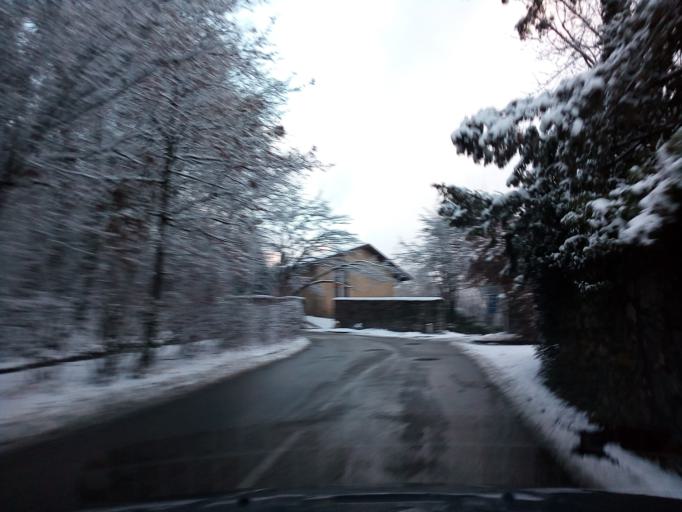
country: FR
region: Rhone-Alpes
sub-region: Departement de l'Isere
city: Corenc
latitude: 45.2214
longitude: 5.7780
